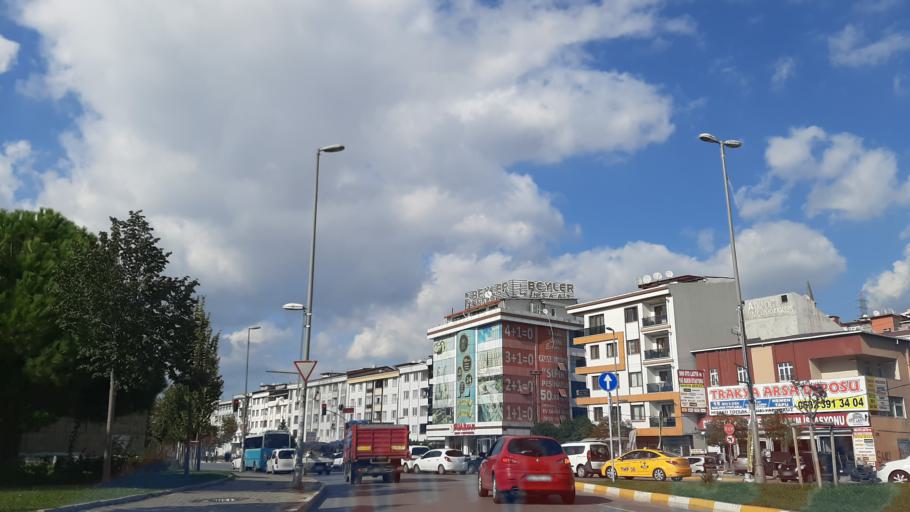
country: TR
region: Istanbul
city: Esenyurt
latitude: 41.0288
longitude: 28.6662
